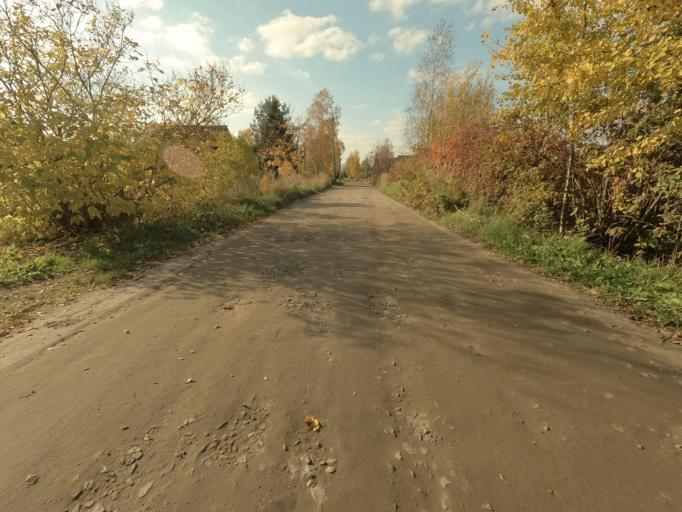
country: RU
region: Leningrad
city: Mga
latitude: 59.7507
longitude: 31.0751
